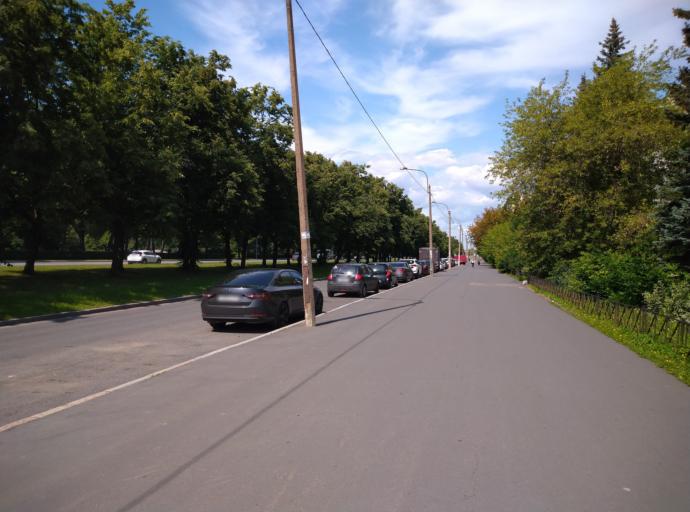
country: RU
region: St.-Petersburg
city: Kupchino
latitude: 59.8591
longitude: 30.3379
